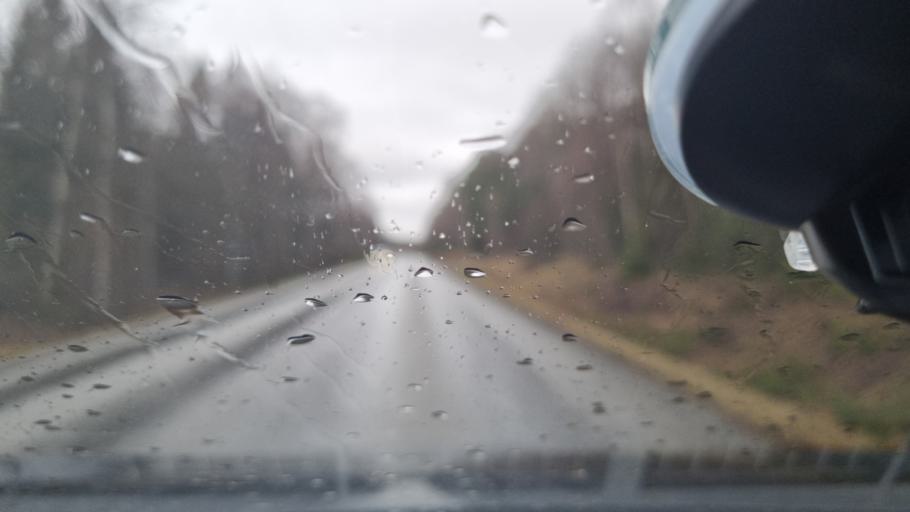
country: SE
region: Stockholm
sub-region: Upplands-Bro Kommun
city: Kungsaengen
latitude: 59.5422
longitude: 17.7401
